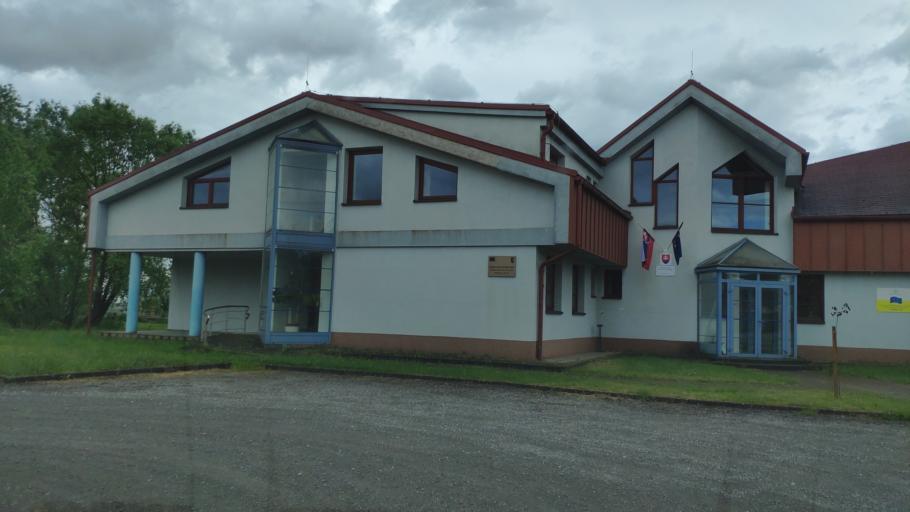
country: SK
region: Kosicky
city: Moldava nad Bodvou
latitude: 48.5762
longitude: 21.1212
